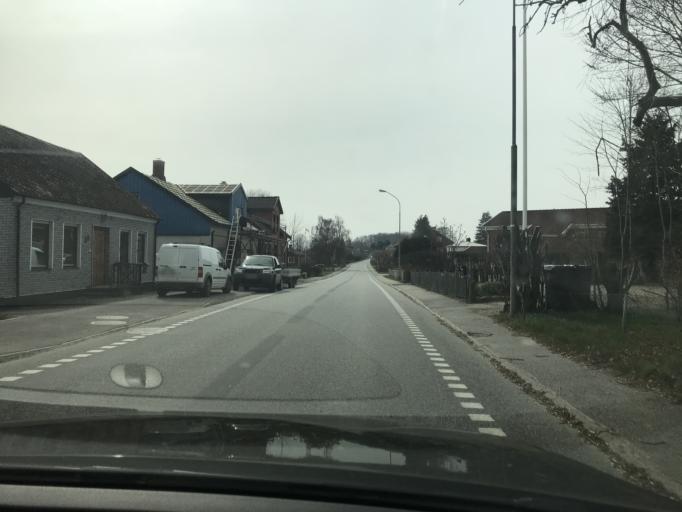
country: SE
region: Skane
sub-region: Skurups Kommun
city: Skivarp
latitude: 55.4246
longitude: 13.5784
